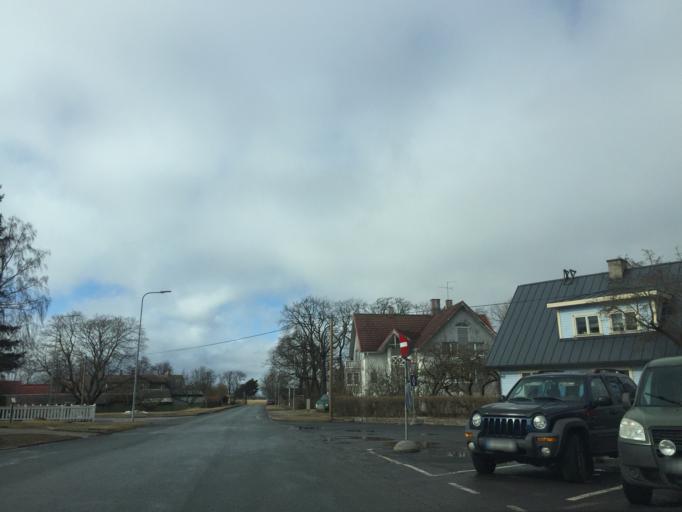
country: EE
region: Laeaene
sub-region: Haapsalu linn
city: Haapsalu
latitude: 58.9482
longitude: 23.5294
